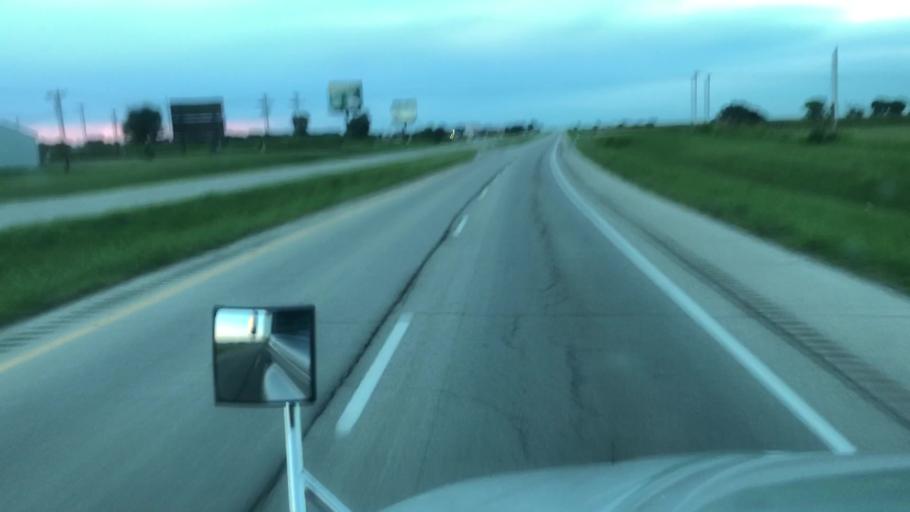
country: US
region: Oklahoma
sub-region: Kay County
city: Ponca City
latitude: 36.7804
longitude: -97.0672
